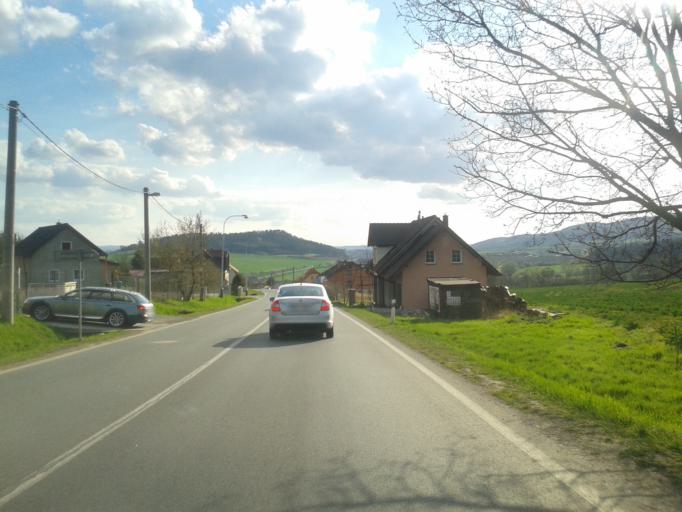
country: CZ
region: Central Bohemia
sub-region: Okres Beroun
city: Kraluv Dvur
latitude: 49.9330
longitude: 14.0081
